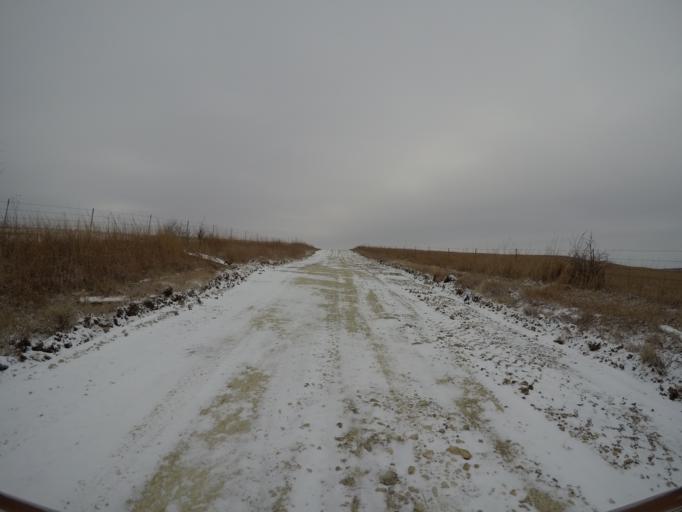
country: US
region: Kansas
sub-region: Wabaunsee County
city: Alma
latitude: 38.8702
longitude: -96.1135
